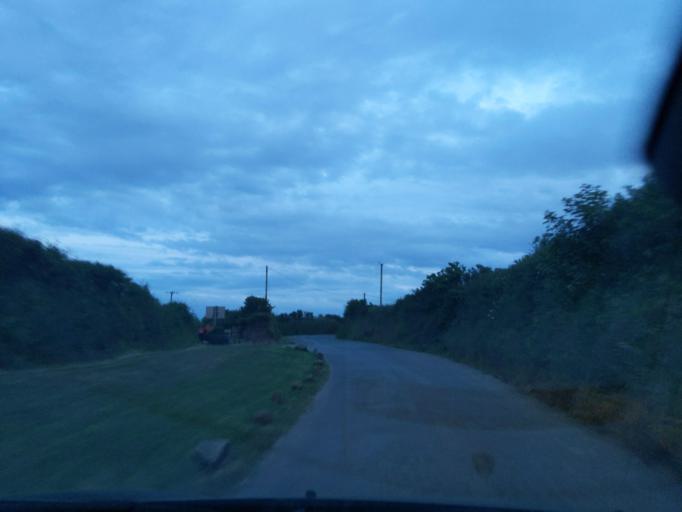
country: GB
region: England
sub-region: Cornwall
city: Wadebridge
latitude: 50.5763
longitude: -4.8303
